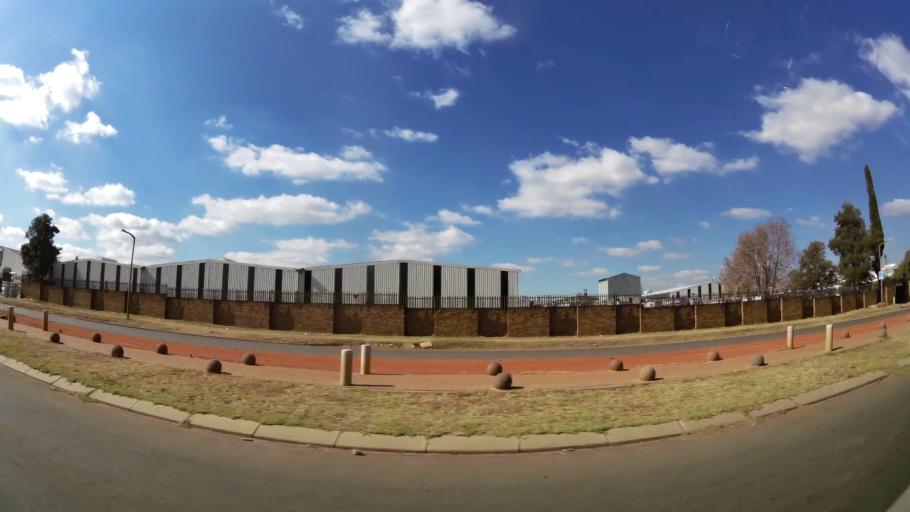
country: ZA
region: Gauteng
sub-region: West Rand District Municipality
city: Krugersdorp
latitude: -26.1485
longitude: 27.7891
